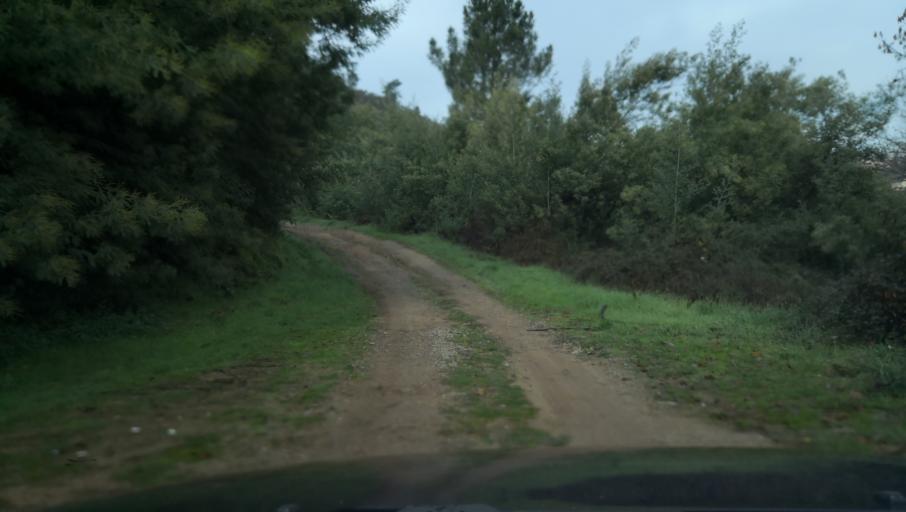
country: PT
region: Vila Real
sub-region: Vila Real
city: Vila Real
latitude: 41.2907
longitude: -7.7496
